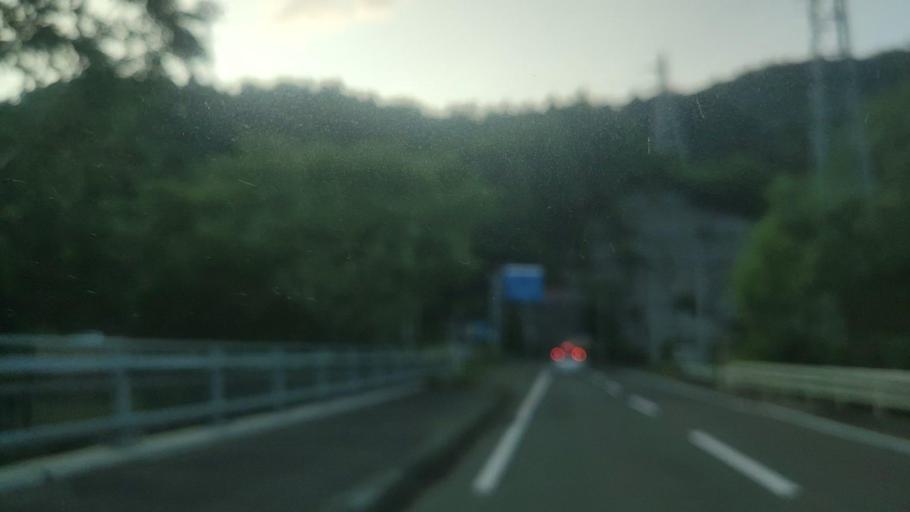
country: JP
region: Hokkaido
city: Bibai
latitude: 43.2451
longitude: 142.0200
